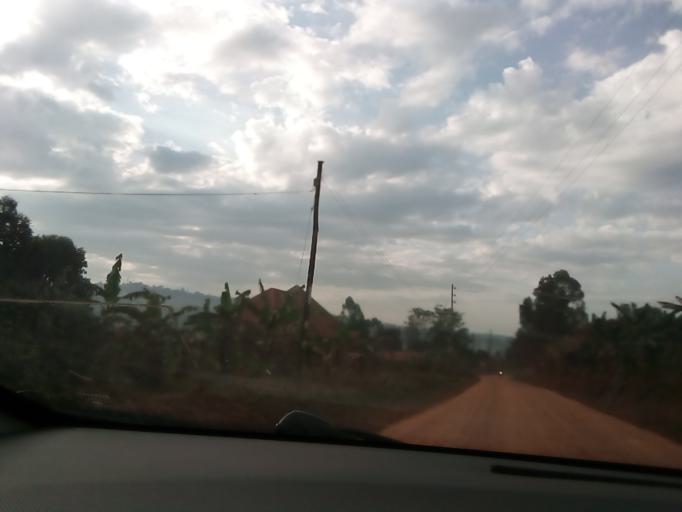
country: UG
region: Central Region
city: Masaka
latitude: -0.3527
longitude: 31.7201
